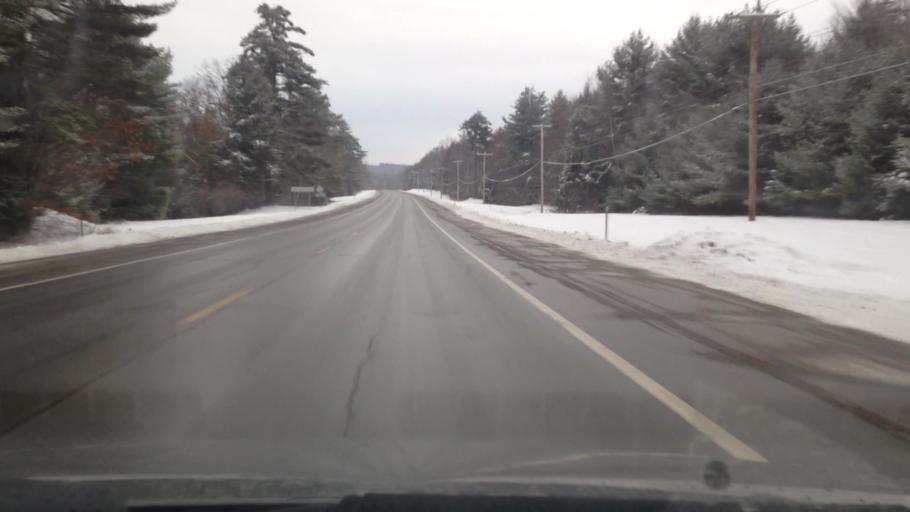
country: US
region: New Hampshire
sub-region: Cheshire County
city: Keene
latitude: 42.9888
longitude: -72.2582
